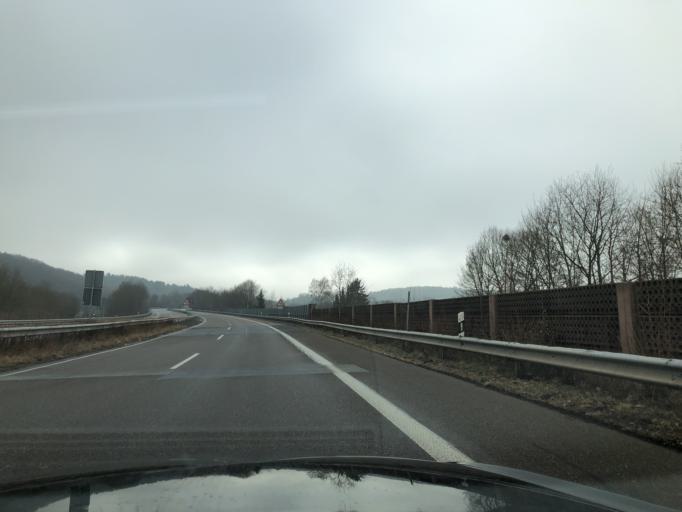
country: DE
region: Rheinland-Pfalz
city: Remagen
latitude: 50.5450
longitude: 7.1970
